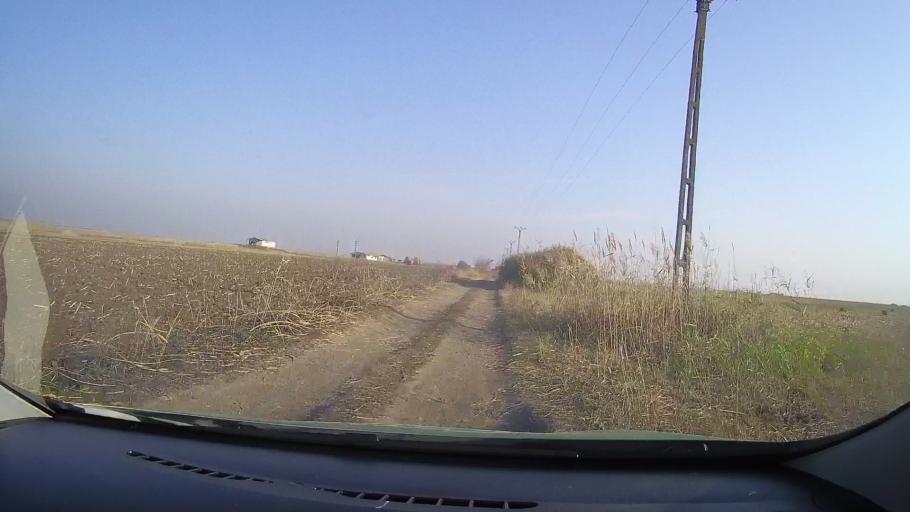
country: RO
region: Arad
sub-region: Comuna Pilu
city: Pilu
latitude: 46.5426
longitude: 21.3287
